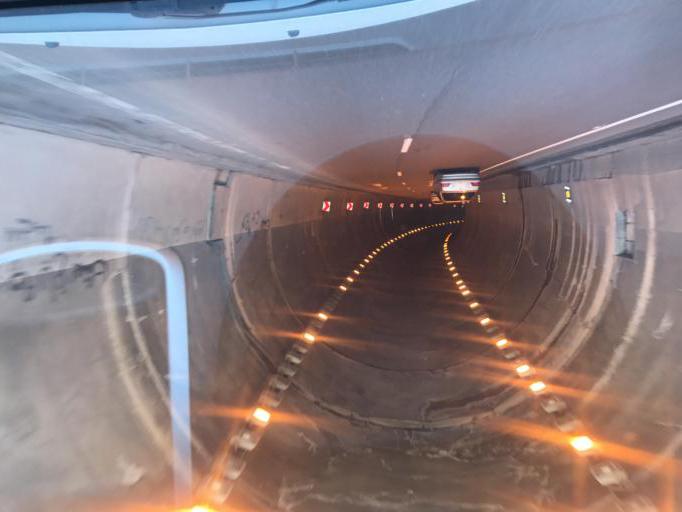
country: IR
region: Gilan
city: Pa'in-e Bazar-e Rudbar
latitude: 36.9519
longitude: 49.5491
